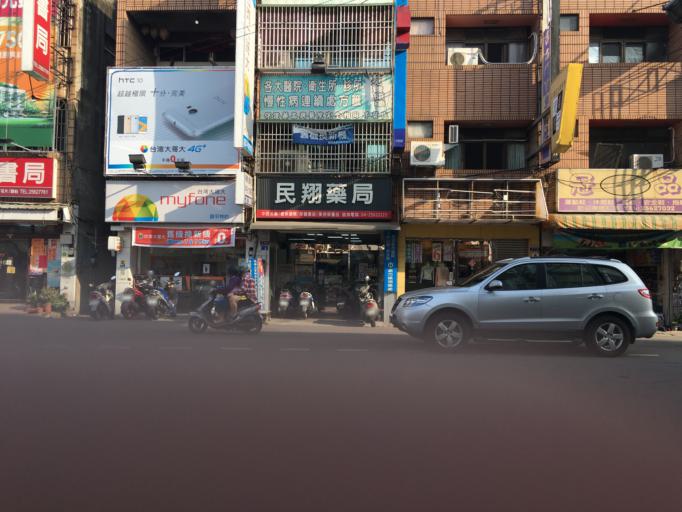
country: TW
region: Taiwan
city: Fengyuan
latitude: 24.2465
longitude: 120.6849
